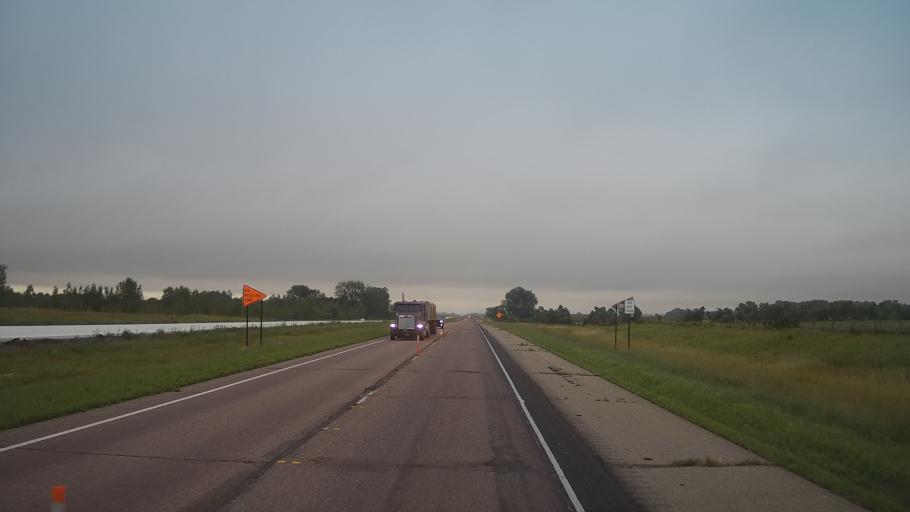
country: US
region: Minnesota
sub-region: Faribault County
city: Winnebago
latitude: 43.6662
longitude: -94.2849
